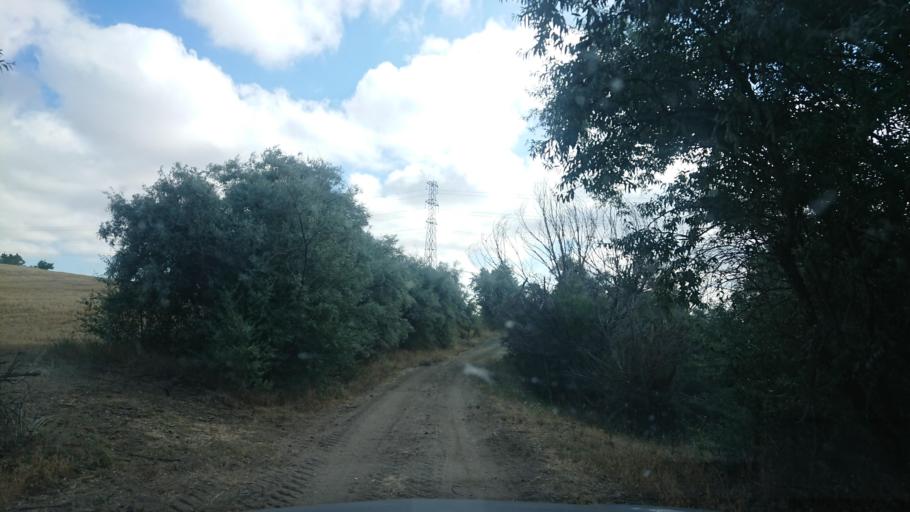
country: TR
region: Aksaray
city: Agacoren
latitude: 38.8591
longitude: 33.9382
